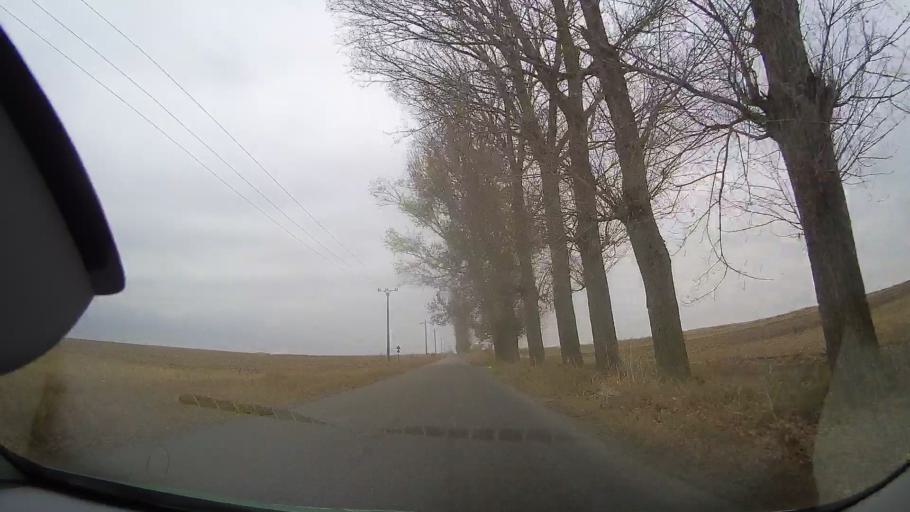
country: RO
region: Buzau
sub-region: Comuna Pogoanele
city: Pogoanele
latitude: 44.9645
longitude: 27.0225
